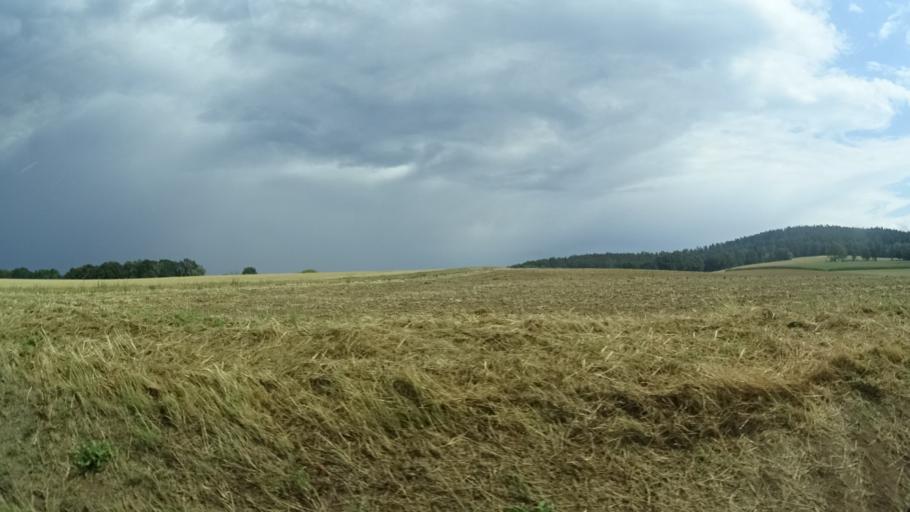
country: DE
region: Hesse
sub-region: Regierungsbezirk Kassel
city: Niederaula
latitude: 50.8065
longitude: 9.6411
